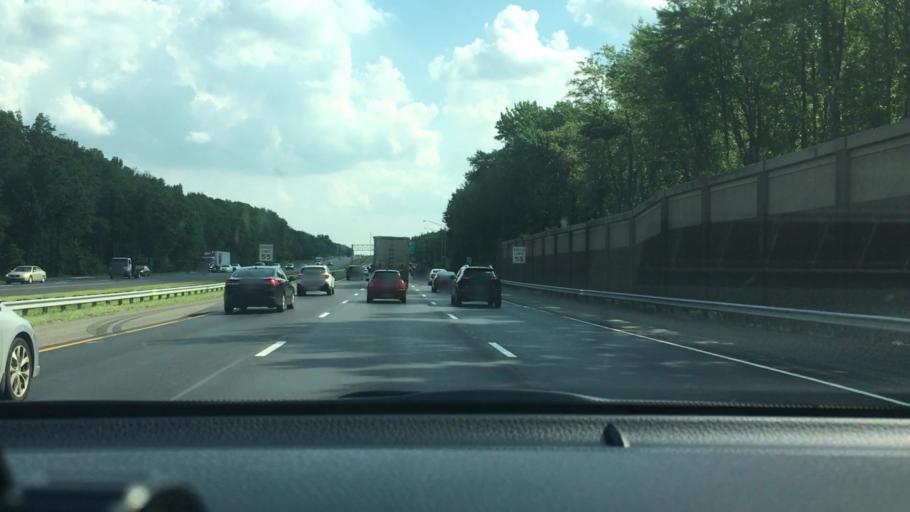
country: US
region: New Jersey
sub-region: Camden County
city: Kingston Estates
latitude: 39.9159
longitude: -74.9814
